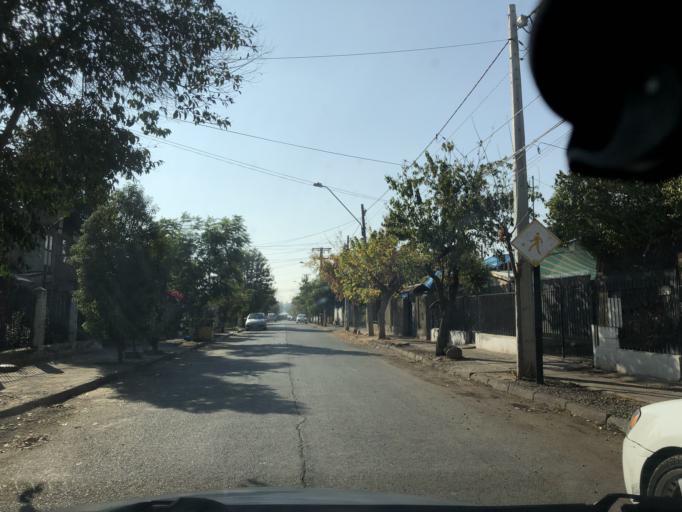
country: CL
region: Santiago Metropolitan
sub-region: Provincia de Cordillera
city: Puente Alto
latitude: -33.6188
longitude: -70.5652
